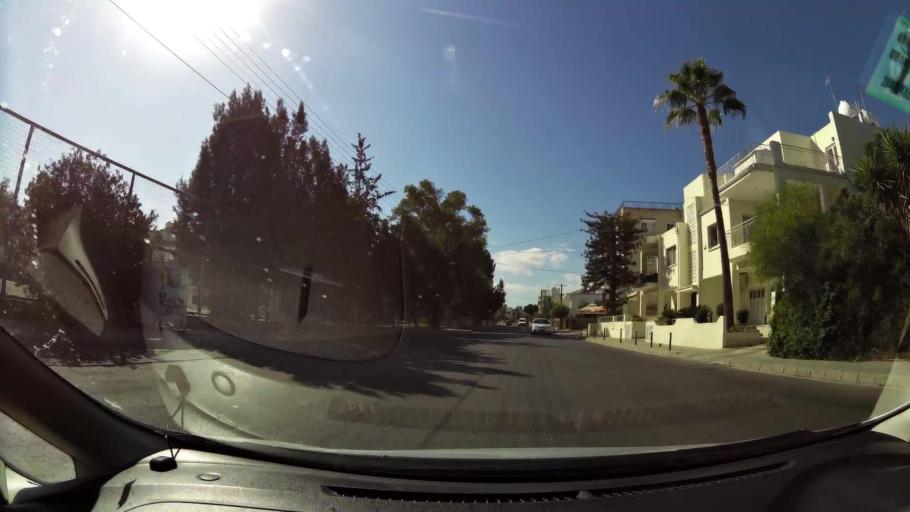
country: CY
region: Lefkosia
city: Nicosia
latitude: 35.1374
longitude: 33.3365
